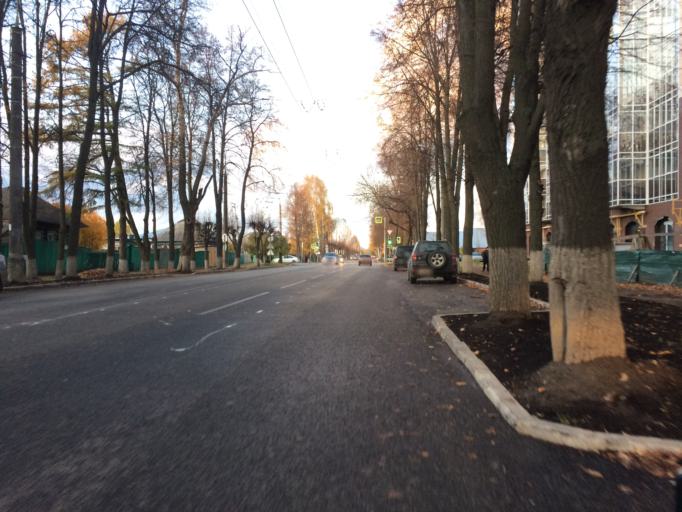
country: RU
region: Mariy-El
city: Yoshkar-Ola
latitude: 56.6494
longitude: 47.8945
